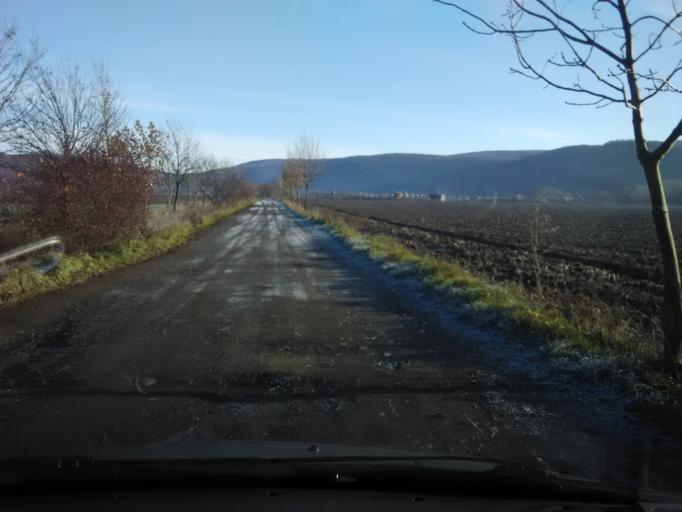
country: SK
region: Nitriansky
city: Tlmace
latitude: 48.3256
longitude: 18.5387
